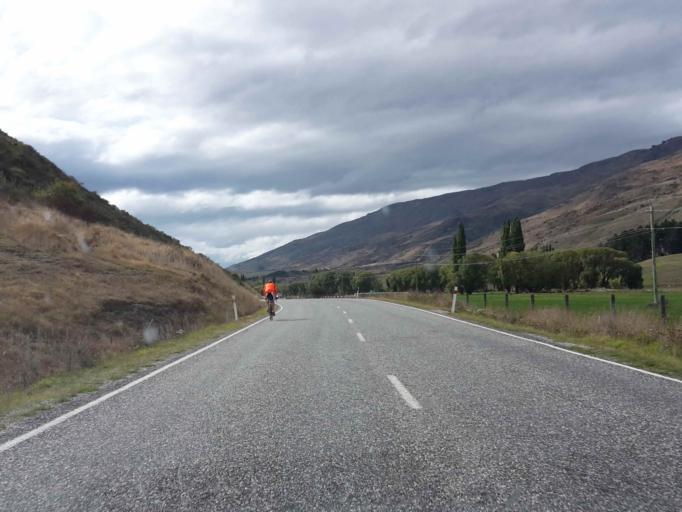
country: NZ
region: Otago
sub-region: Queenstown-Lakes District
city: Wanaka
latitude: -44.8481
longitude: 169.0432
